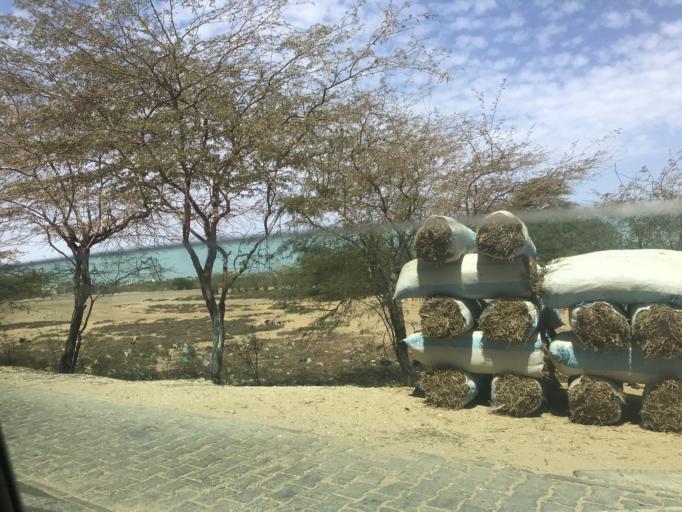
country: SN
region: Saint-Louis
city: Saint-Louis
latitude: 16.0303
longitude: -16.4734
